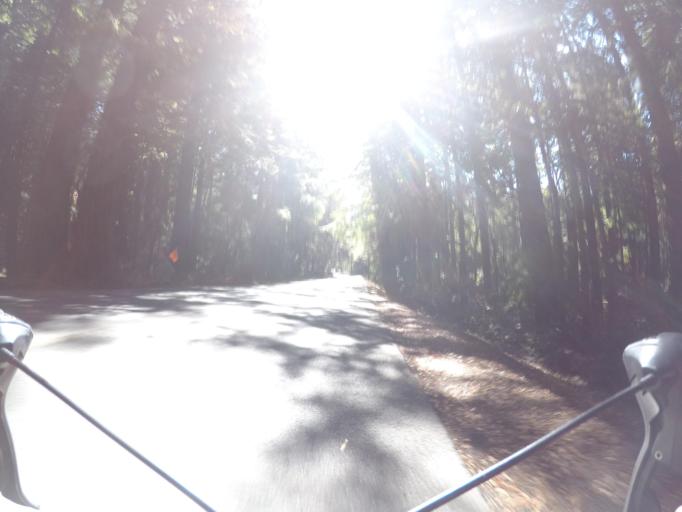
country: US
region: California
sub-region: San Mateo County
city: Portola Valley
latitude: 37.2777
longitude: -122.2930
